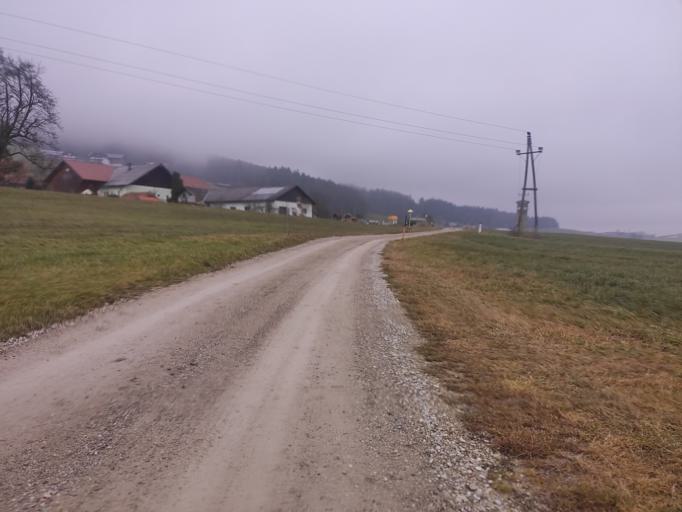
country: AT
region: Salzburg
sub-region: Politischer Bezirk Salzburg-Umgebung
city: Schleedorf
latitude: 47.9541
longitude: 13.1245
